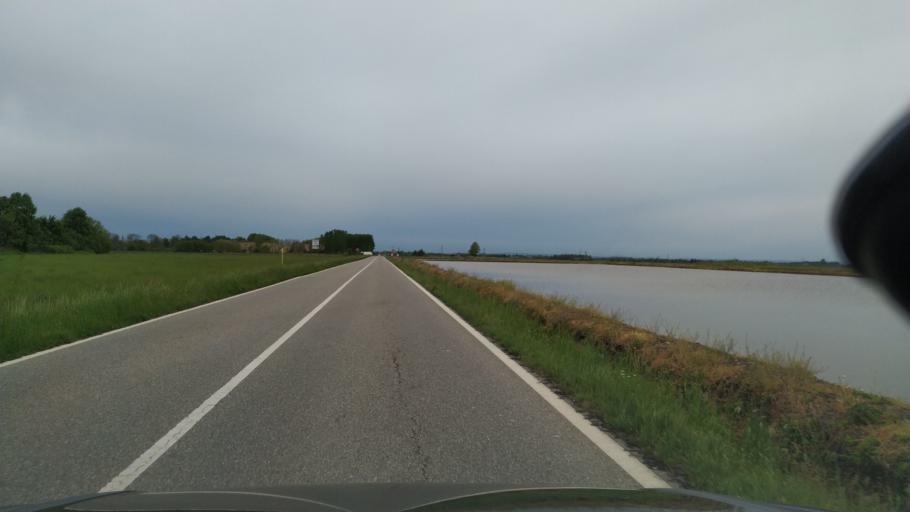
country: IT
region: Piedmont
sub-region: Provincia di Vercelli
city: Arborio
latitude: 45.4822
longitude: 8.3881
